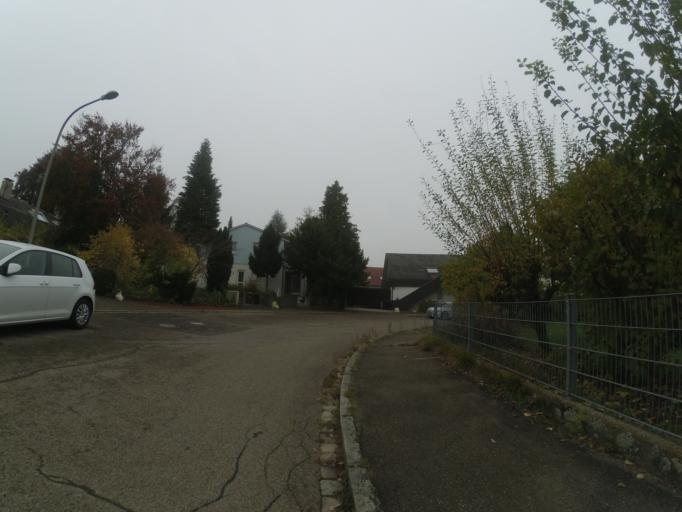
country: DE
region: Baden-Wuerttemberg
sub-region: Tuebingen Region
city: Ulm
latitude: 48.3812
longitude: 9.9605
